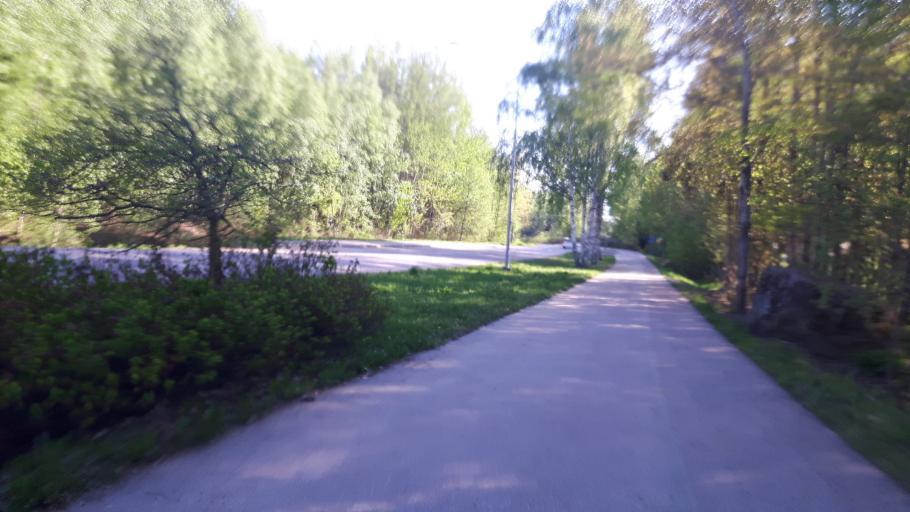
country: FI
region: Kymenlaakso
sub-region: Kotka-Hamina
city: Kotka
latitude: 60.4386
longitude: 26.8828
